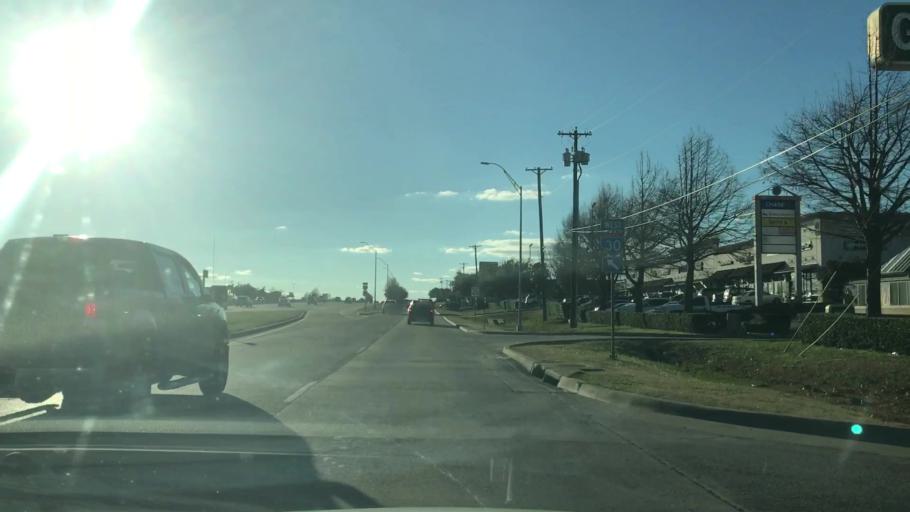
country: US
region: Texas
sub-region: Rockwall County
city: Rockwall
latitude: 32.8995
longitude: -96.4643
